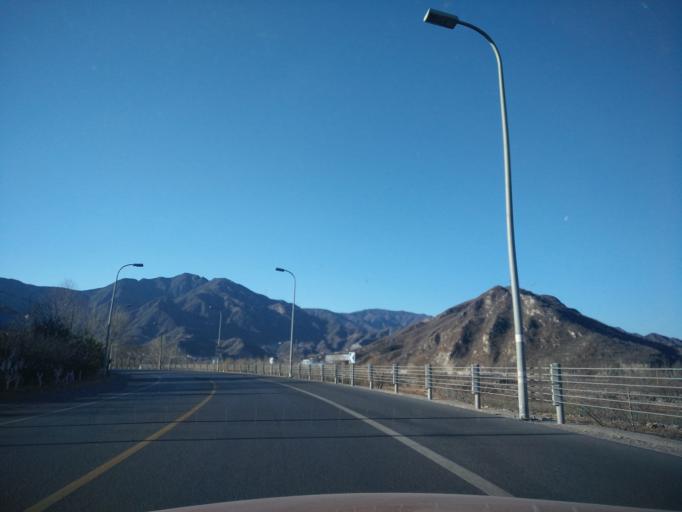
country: CN
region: Beijing
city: Miaofengshan
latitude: 39.9864
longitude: 116.0614
